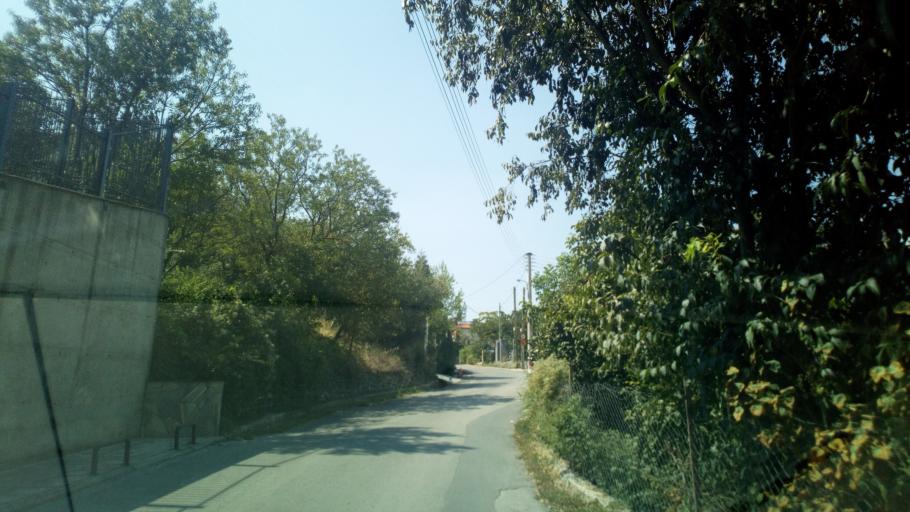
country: GR
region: Central Macedonia
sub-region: Nomos Thessalonikis
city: Asvestochori
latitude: 40.6391
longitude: 23.0213
